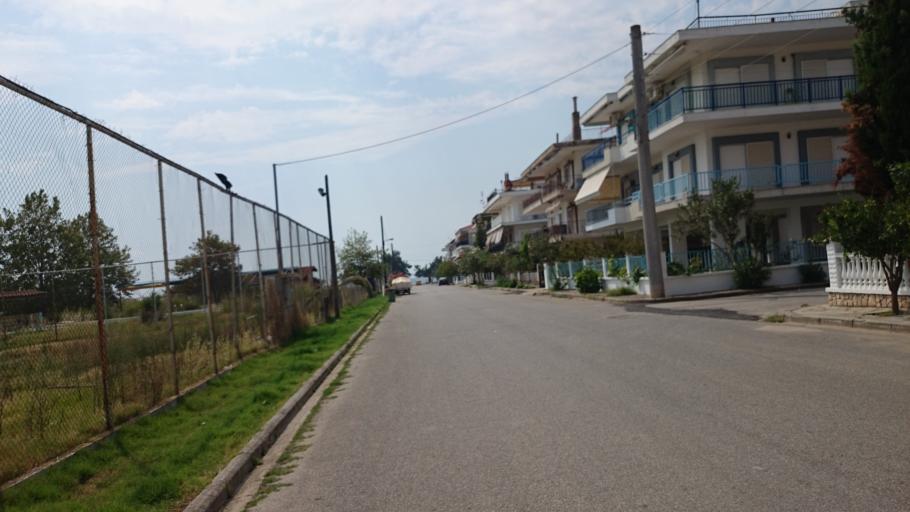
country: GR
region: Central Macedonia
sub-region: Nomos Chalkidikis
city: Nea Moudhania
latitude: 40.2507
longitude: 23.2543
